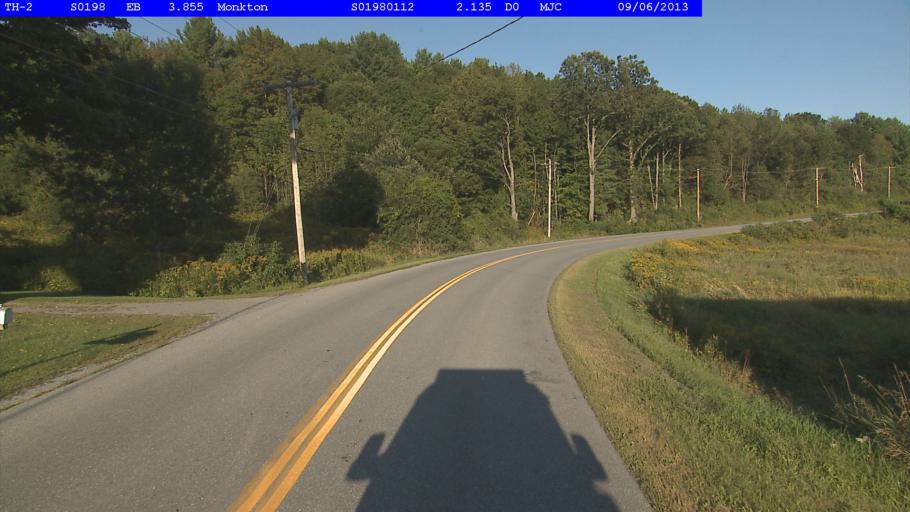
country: US
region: Vermont
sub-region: Chittenden County
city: Hinesburg
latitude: 44.2433
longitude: -73.1593
